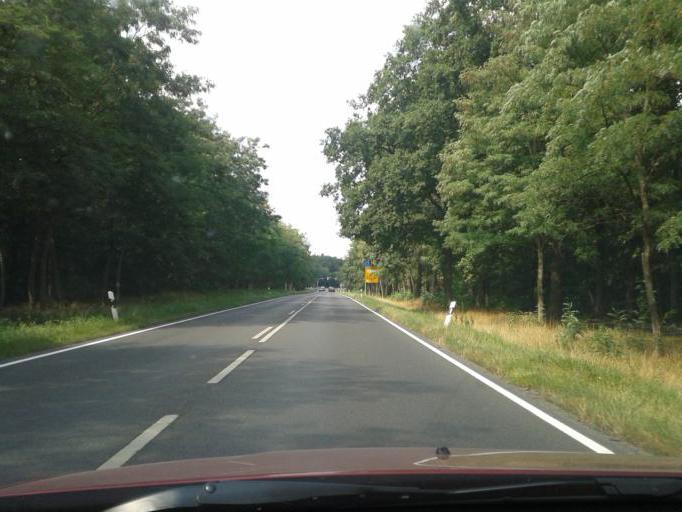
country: DE
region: Brandenburg
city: Birkenwerder
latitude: 52.7101
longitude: 13.2629
